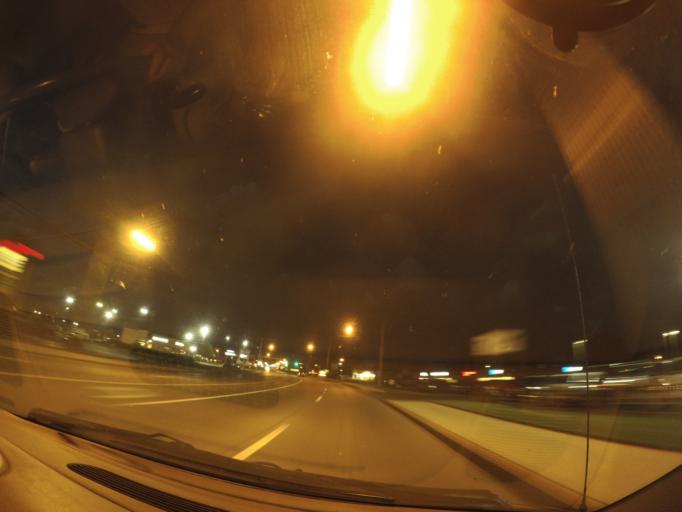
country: US
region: Ohio
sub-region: Ashtabula County
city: Edgewood
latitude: 41.8766
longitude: -80.7590
